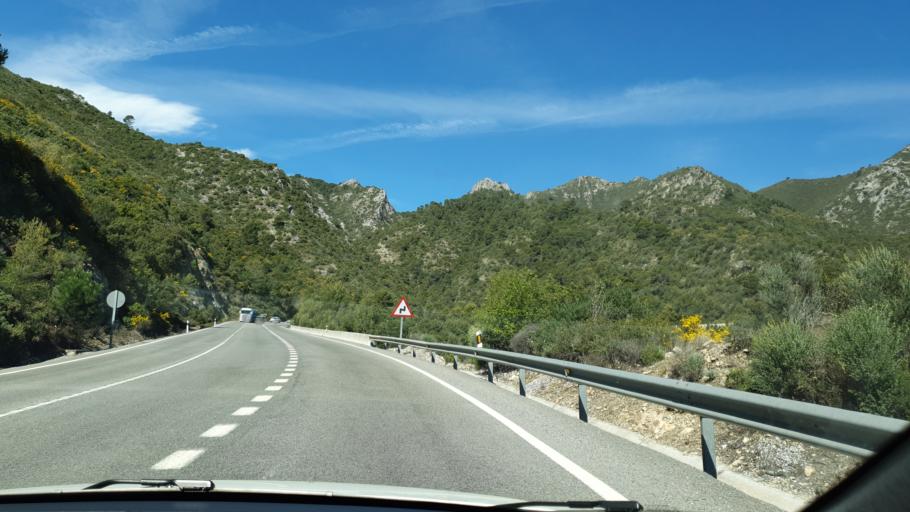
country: ES
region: Andalusia
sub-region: Provincia de Malaga
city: Ojen
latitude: 36.5660
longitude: -4.8623
